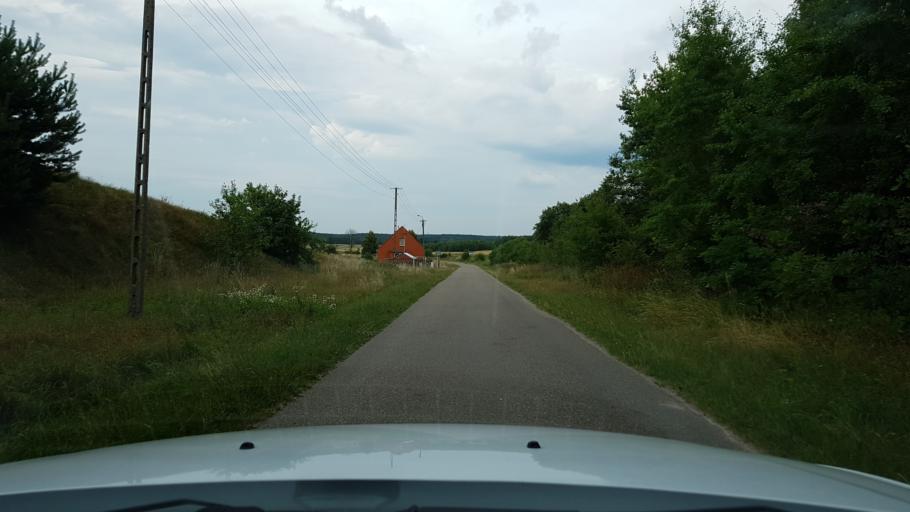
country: PL
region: West Pomeranian Voivodeship
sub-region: Powiat drawski
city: Wierzchowo
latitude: 53.4636
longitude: 16.1080
